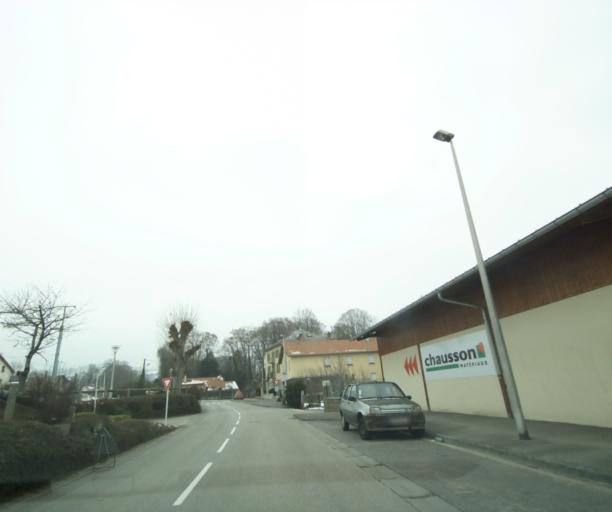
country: FR
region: Rhone-Alpes
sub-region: Departement de la Haute-Savoie
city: Reignier-Esery
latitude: 46.1260
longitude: 6.2673
